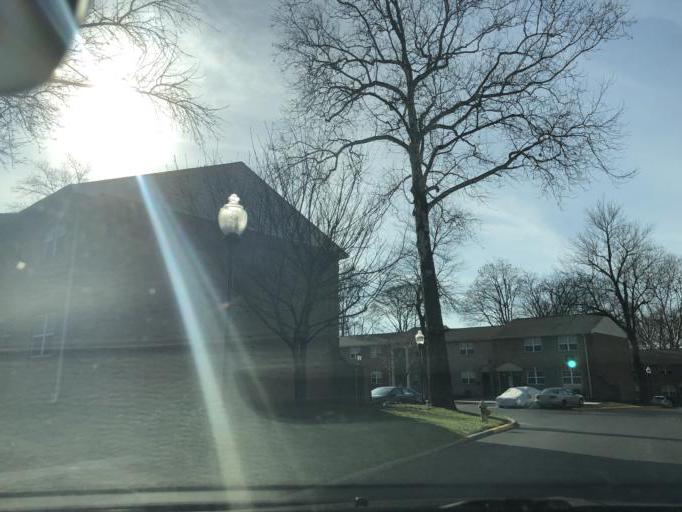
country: US
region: New Jersey
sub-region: Burlington County
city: Moorestown-Lenola
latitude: 39.9591
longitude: -74.9740
